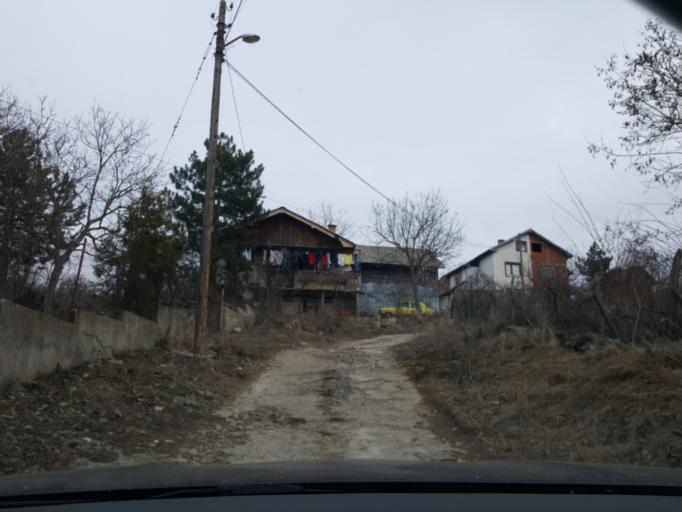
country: RS
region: Central Serbia
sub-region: Pirotski Okrug
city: Dimitrovgrad
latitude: 43.0090
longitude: 22.7587
